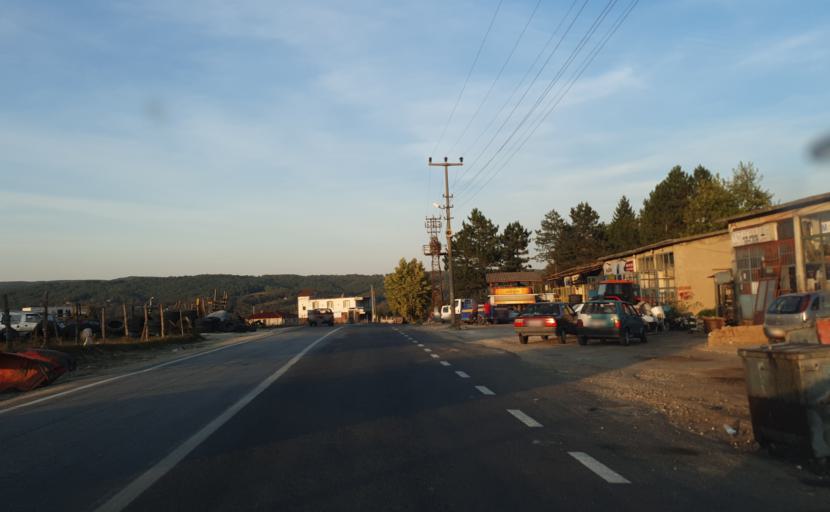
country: TR
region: Kirklareli
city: Sergen
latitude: 41.8283
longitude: 27.7784
